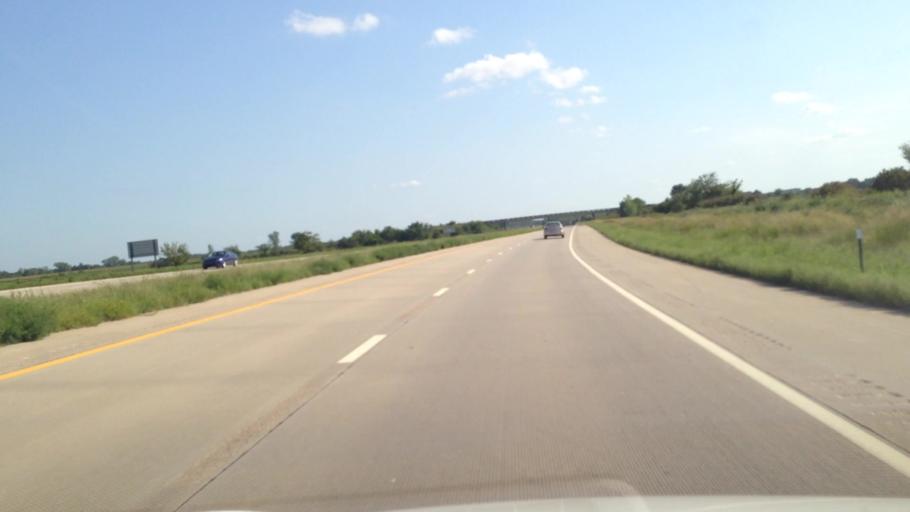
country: US
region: Kansas
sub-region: Bourbon County
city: Fort Scott
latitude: 37.9265
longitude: -94.7047
